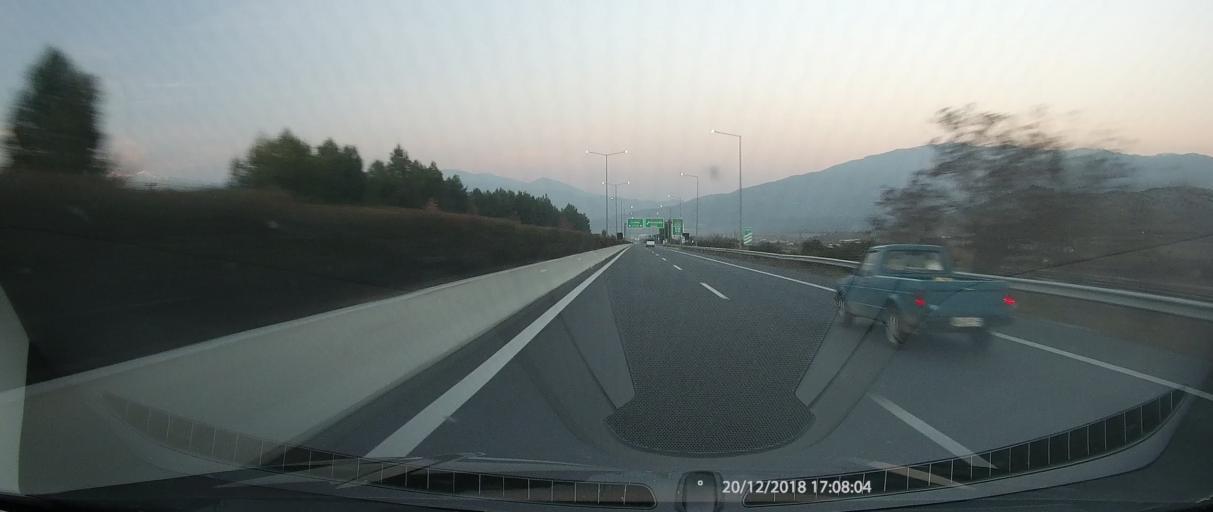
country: GR
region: Thessaly
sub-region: Nomos Larisis
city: Makrychori
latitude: 39.7910
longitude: 22.4953
